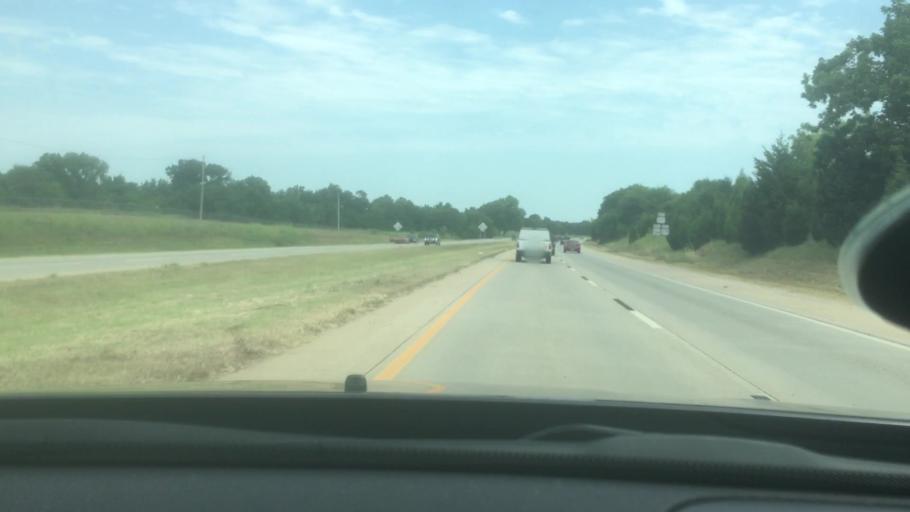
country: US
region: Oklahoma
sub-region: Pottawatomie County
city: Tecumseh
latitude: 35.2904
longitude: -96.9422
